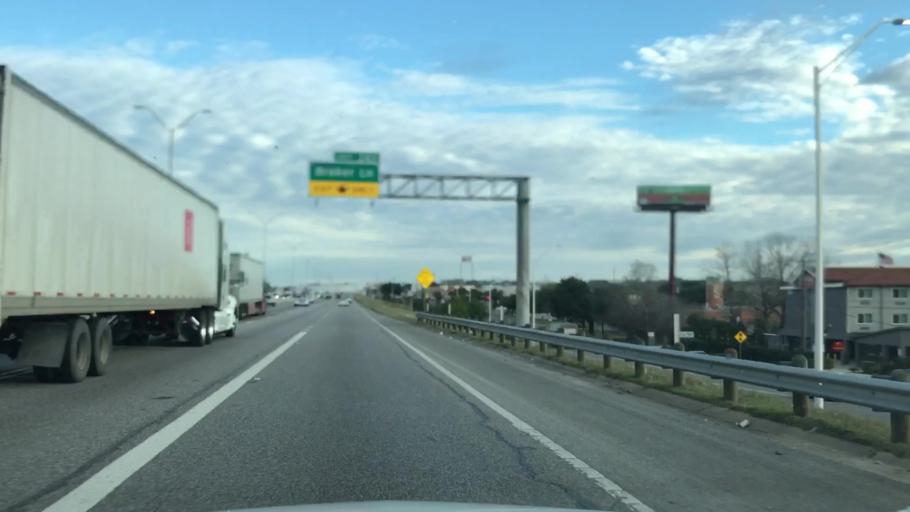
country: US
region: Texas
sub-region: Travis County
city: Wells Branch
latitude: 30.3553
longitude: -97.6897
